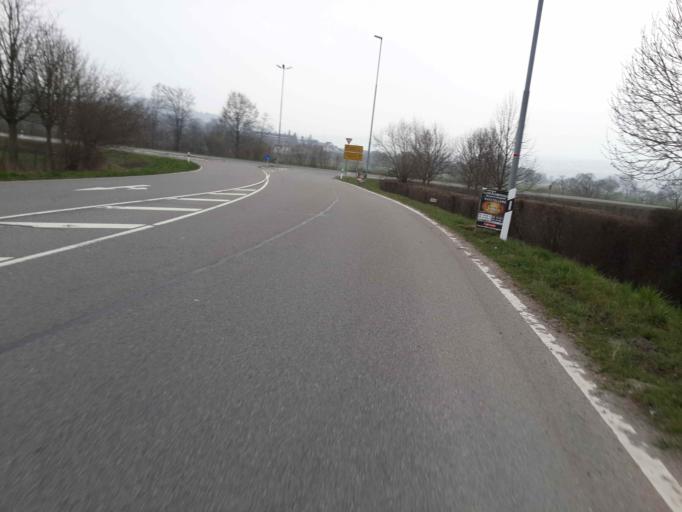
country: DE
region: Baden-Wuerttemberg
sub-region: Karlsruhe Region
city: Obrigheim
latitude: 49.3537
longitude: 9.1047
